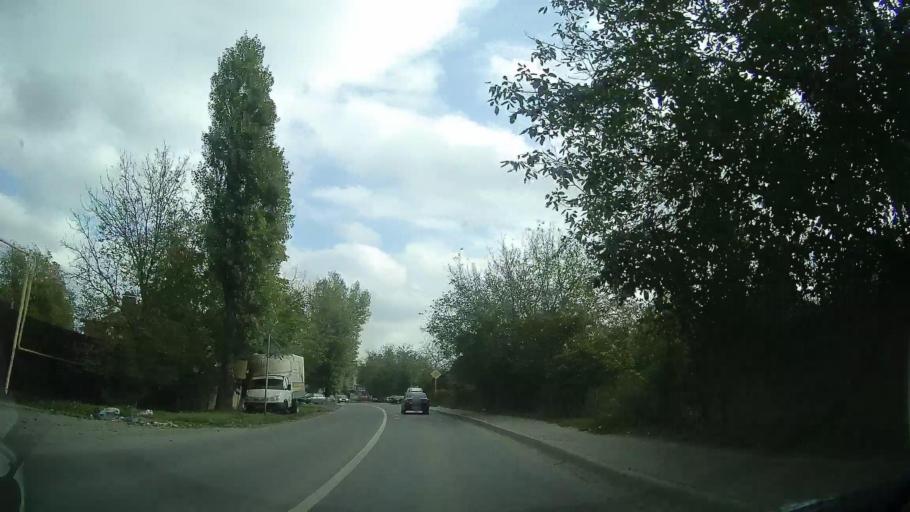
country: RU
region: Rostov
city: Severnyy
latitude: 47.2851
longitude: 39.6678
